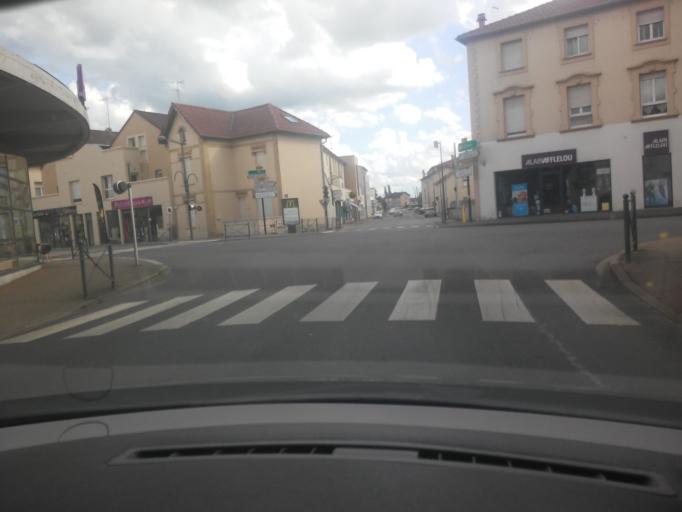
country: FR
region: Lorraine
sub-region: Departement de Meurthe-et-Moselle
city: Jarny
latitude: 49.1581
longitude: 5.8805
